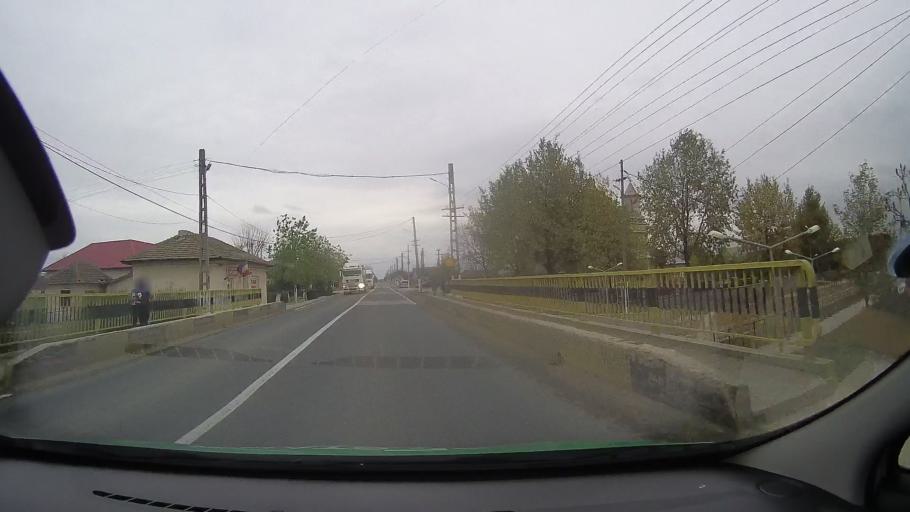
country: RO
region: Constanta
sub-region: Comuna Nicolae Balcescu
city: Nicolae Balcescu
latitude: 44.3882
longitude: 28.3796
